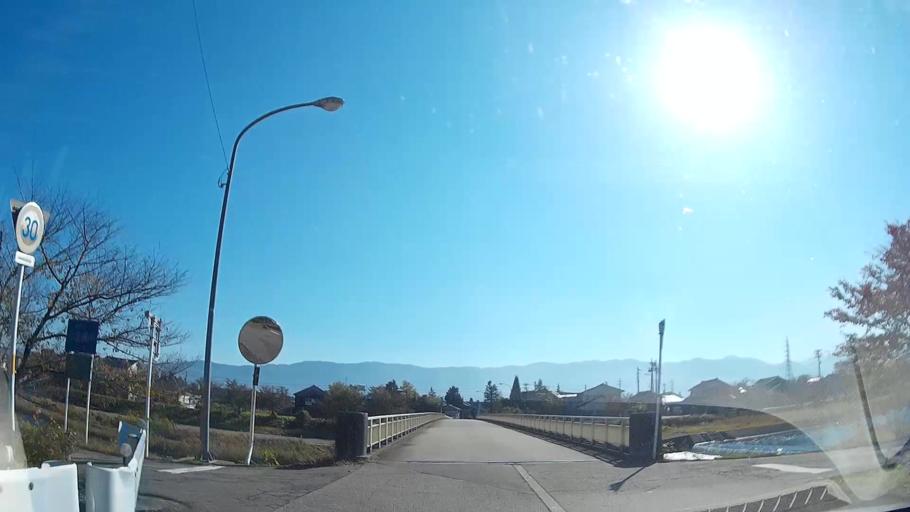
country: JP
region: Toyama
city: Fukumitsu
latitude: 36.5524
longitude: 136.8720
